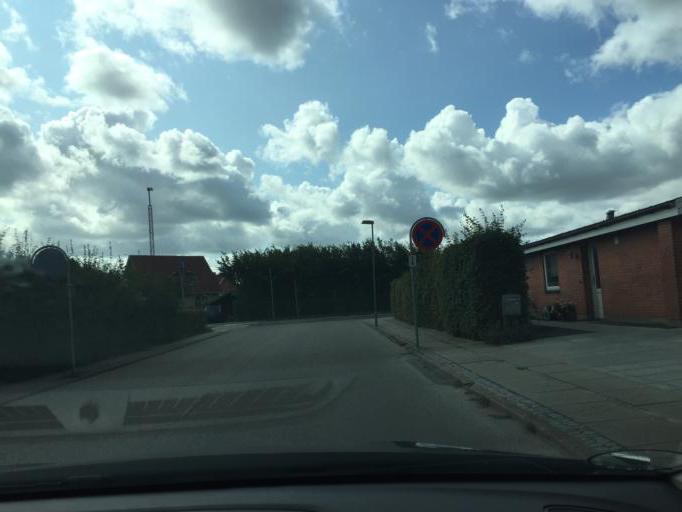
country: DK
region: Central Jutland
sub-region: Odder Kommune
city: Odder
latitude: 55.9773
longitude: 10.1629
